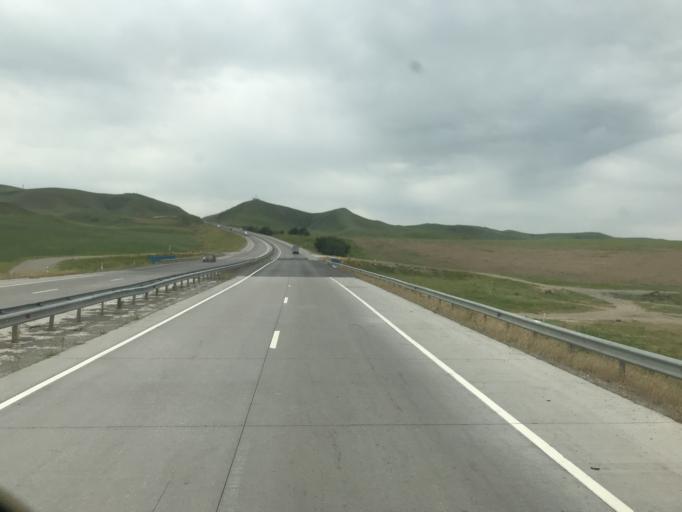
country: KZ
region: Ongtustik Qazaqstan
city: Qazyqurt
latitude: 42.0231
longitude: 69.4694
